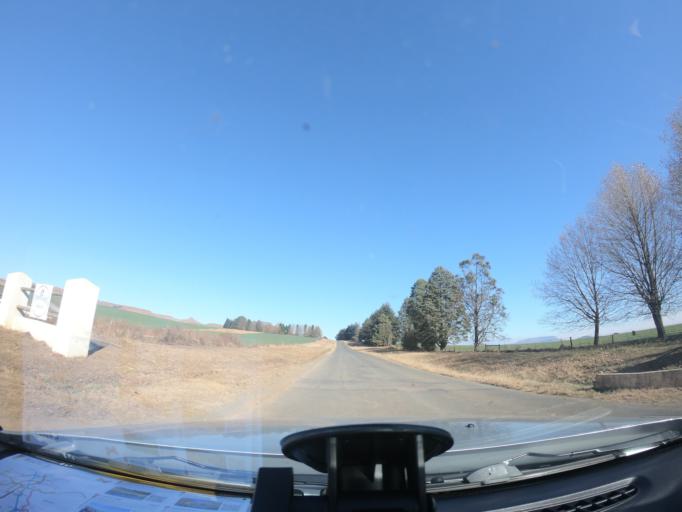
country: ZA
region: KwaZulu-Natal
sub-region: uMgungundlovu District Municipality
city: Mooirivier
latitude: -29.3270
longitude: 29.8275
